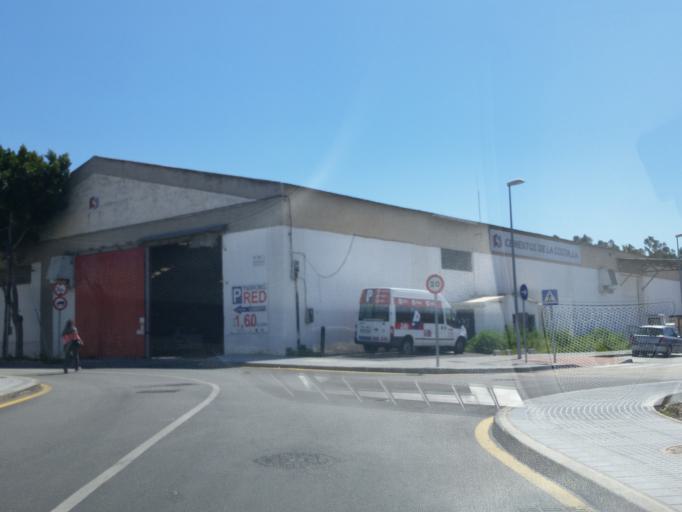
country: ES
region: Andalusia
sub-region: Provincia de Malaga
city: Torremolinos
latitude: 36.6687
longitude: -4.4772
